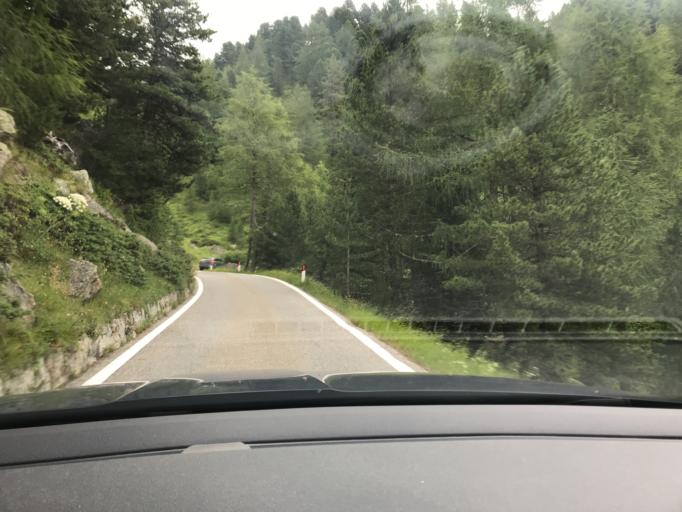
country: IT
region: Trentino-Alto Adige
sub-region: Bolzano
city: San Martino
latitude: 46.8900
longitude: 12.1952
